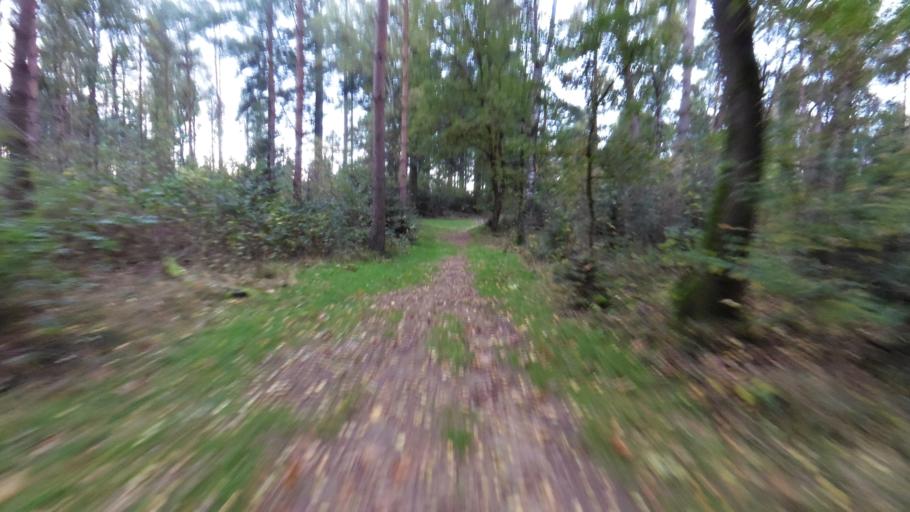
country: NL
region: Gelderland
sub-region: Gemeente Ede
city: Wekerom
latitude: 52.0916
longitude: 5.6736
